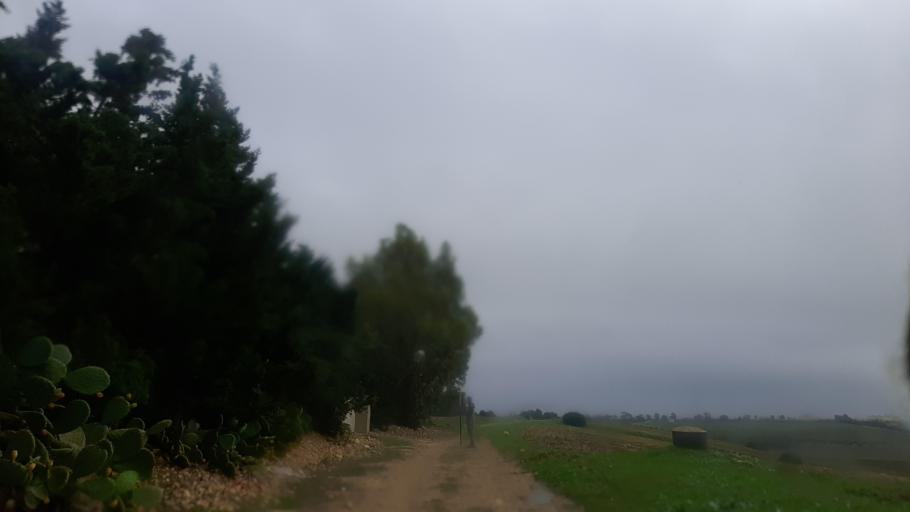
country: TN
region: Nabul
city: Qulaybiyah
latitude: 36.8290
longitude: 11.0328
